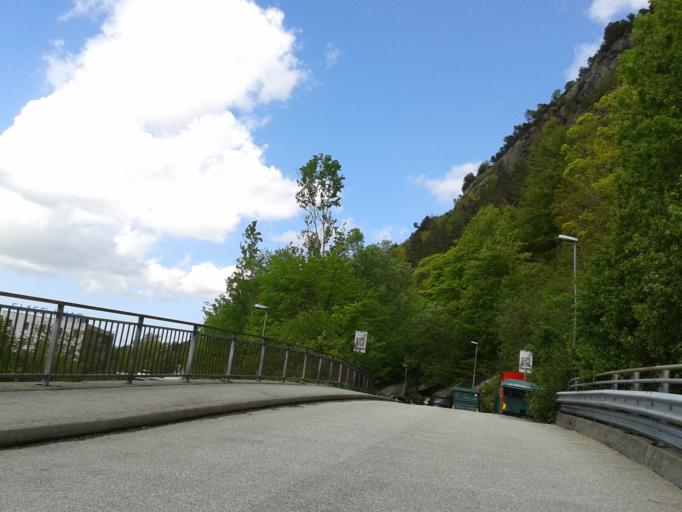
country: NO
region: Hordaland
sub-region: Bergen
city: Bergen
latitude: 60.4147
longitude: 5.3223
